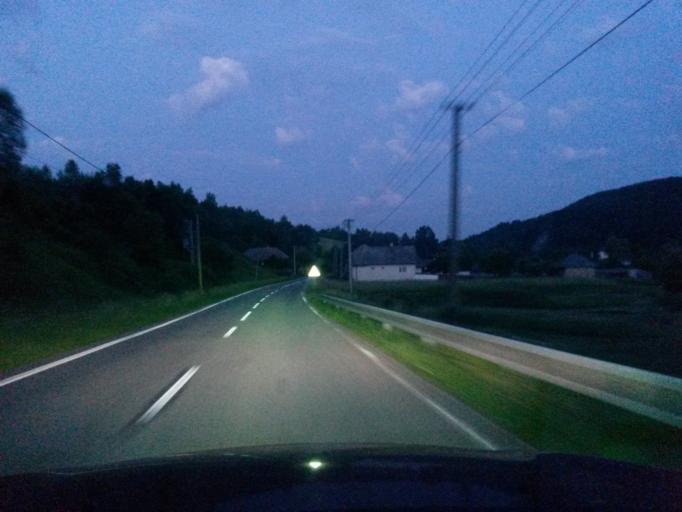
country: UA
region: Zakarpattia
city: Velykyi Bereznyi
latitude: 48.9254
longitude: 22.3141
